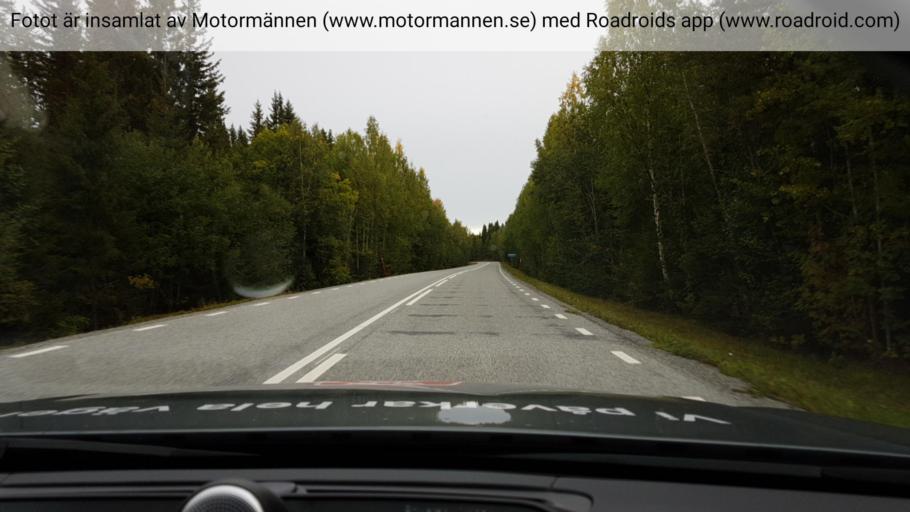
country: SE
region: Jaemtland
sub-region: Stroemsunds Kommun
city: Stroemsund
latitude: 64.1588
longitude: 15.6745
